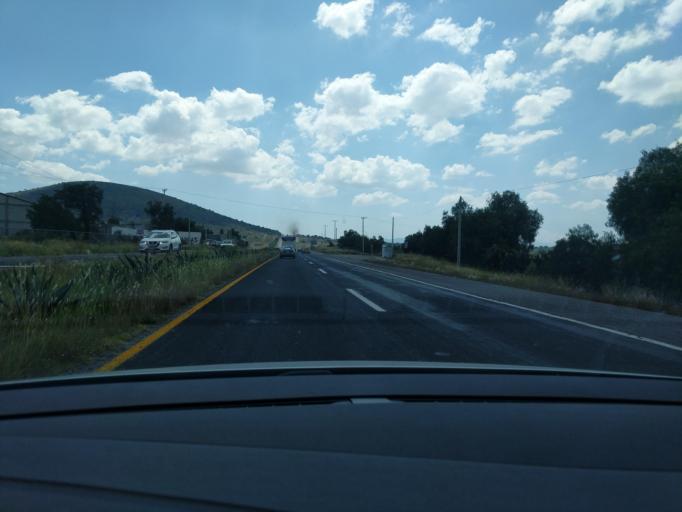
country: MX
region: Hidalgo
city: Zempoala
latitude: 19.9025
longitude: -98.6732
